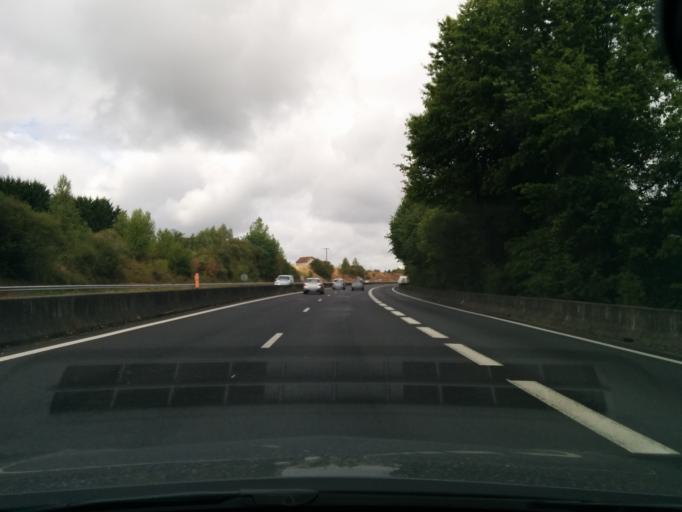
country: FR
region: Limousin
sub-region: Departement de la Correze
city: Donzenac
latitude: 45.2221
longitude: 1.5115
